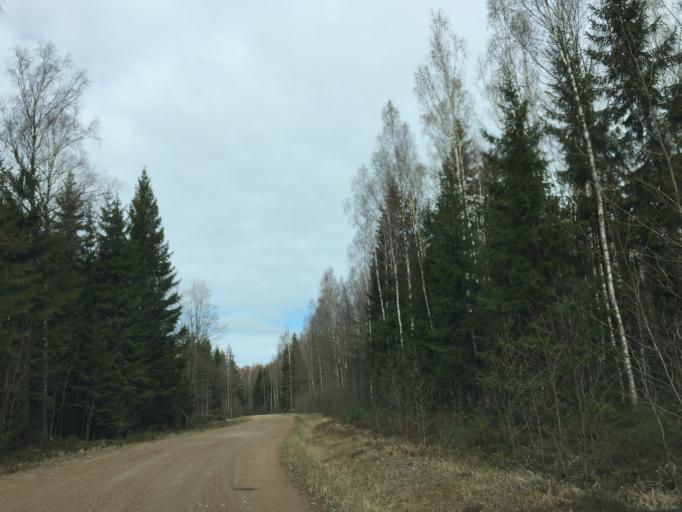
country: LV
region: Saulkrastu
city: Saulkrasti
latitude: 57.5050
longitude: 24.4202
